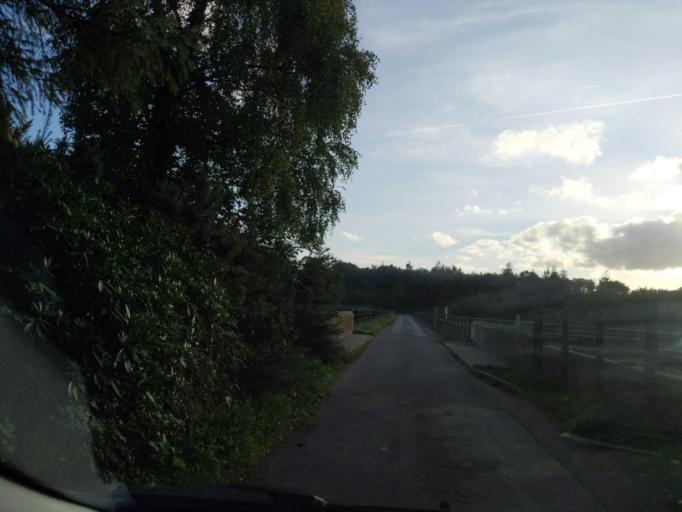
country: GB
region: England
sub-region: Devon
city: Bovey Tracey
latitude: 50.6294
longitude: -3.6880
